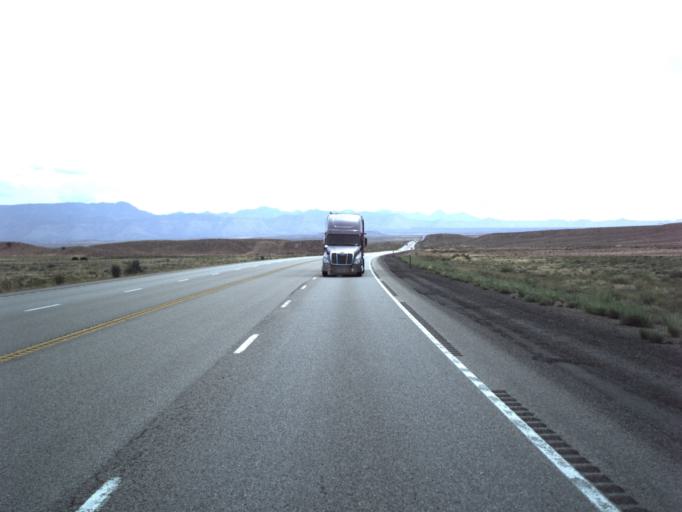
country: US
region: Utah
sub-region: Carbon County
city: Wellington
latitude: 39.5451
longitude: -110.6188
